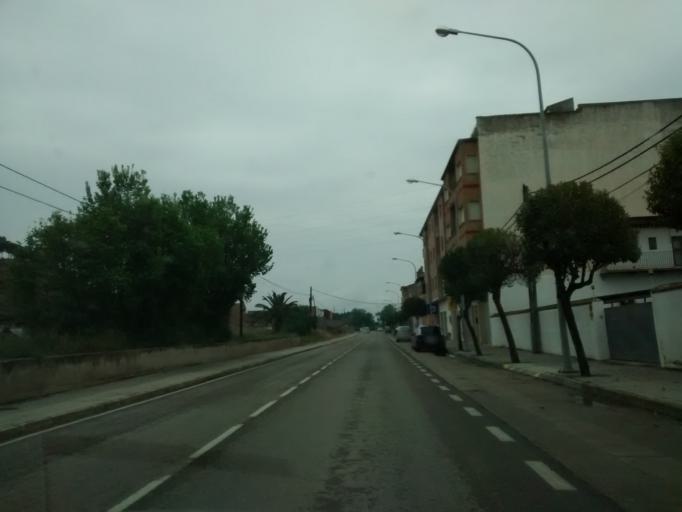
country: ES
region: Aragon
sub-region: Provincia de Zaragoza
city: Caspe
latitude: 41.2285
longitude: -0.0357
